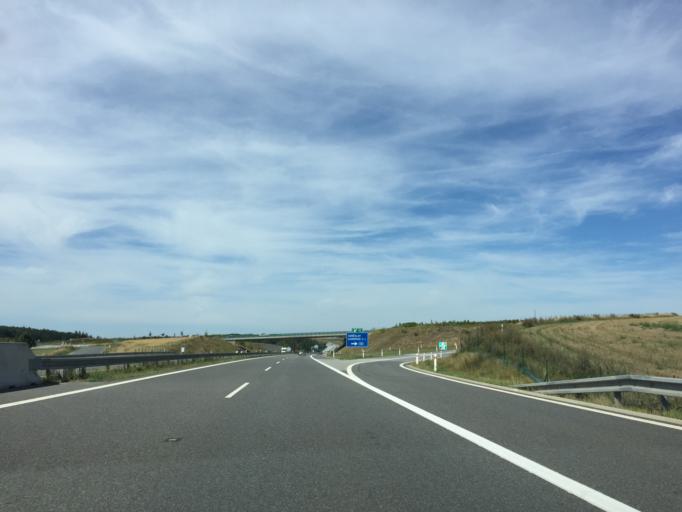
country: CZ
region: Jihocesky
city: Sobeslav
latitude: 49.2649
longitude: 14.7366
